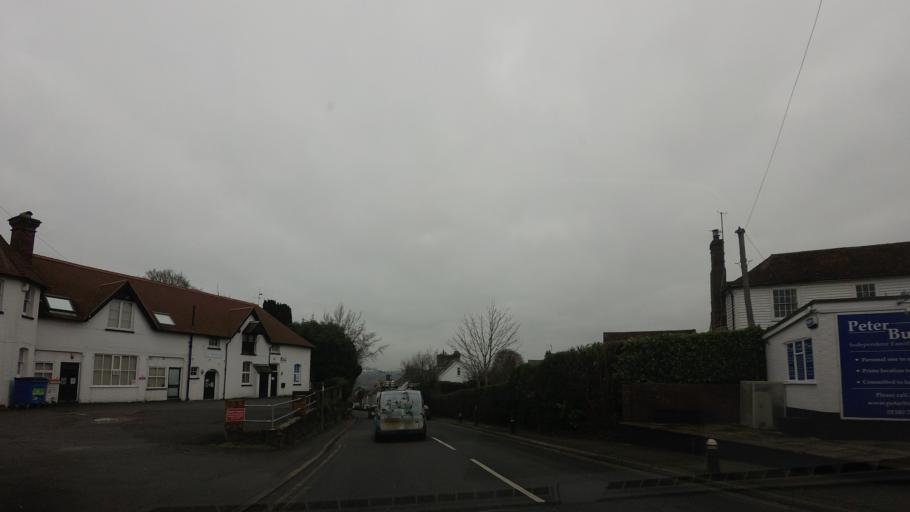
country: GB
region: England
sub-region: Kent
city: Hawkhurst
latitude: 51.0482
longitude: 0.5106
